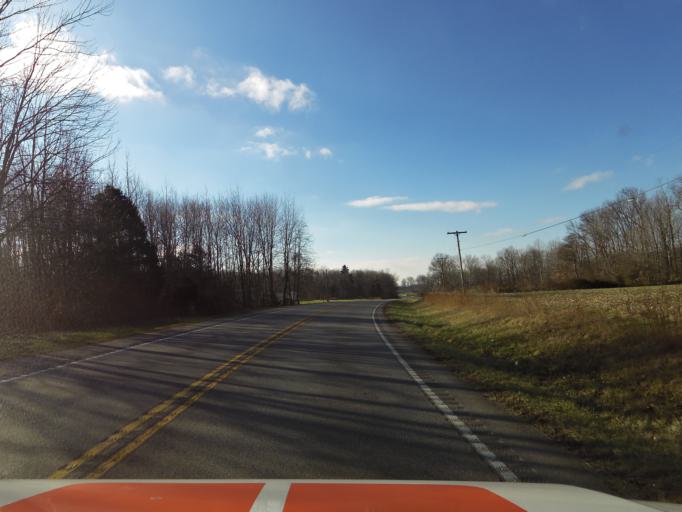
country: US
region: Indiana
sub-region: Jackson County
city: Seymour
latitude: 38.9664
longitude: -85.7907
